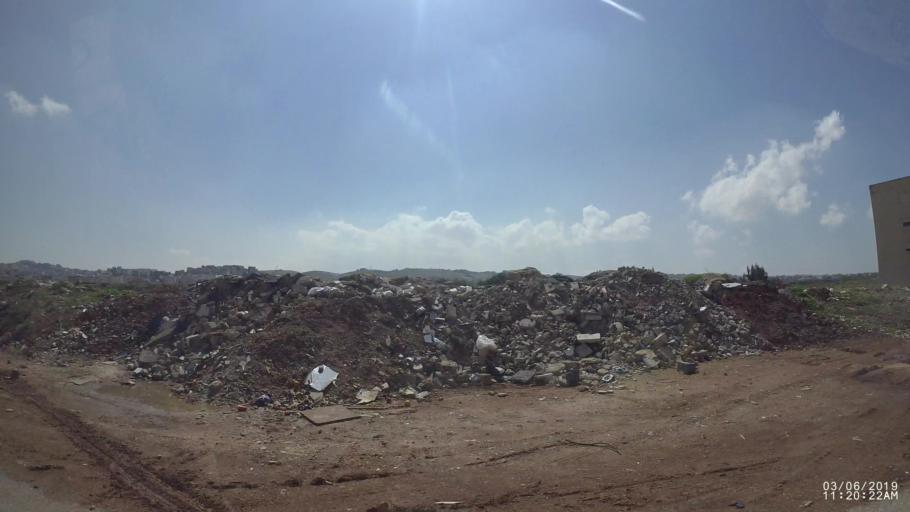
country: JO
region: Amman
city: Amman
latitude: 31.9779
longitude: 35.9983
